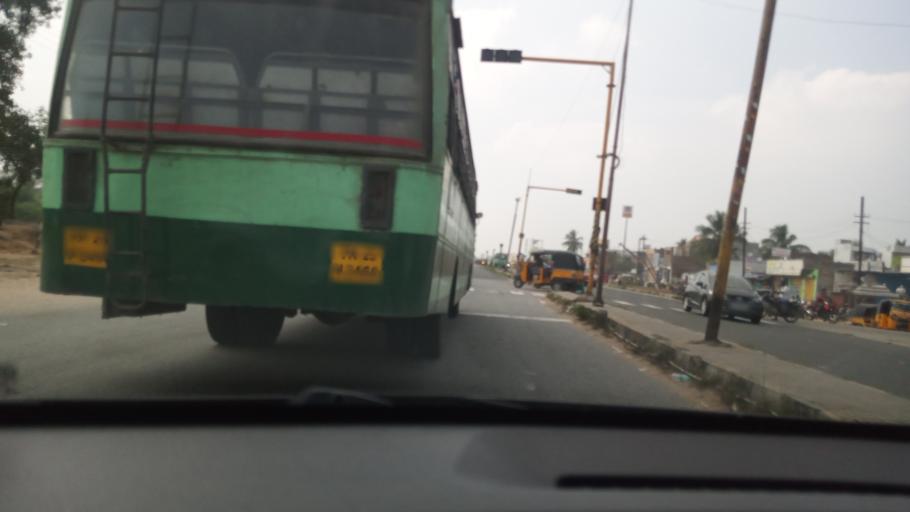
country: IN
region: Tamil Nadu
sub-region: Vellore
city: Walajapet
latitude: 12.8968
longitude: 79.5083
